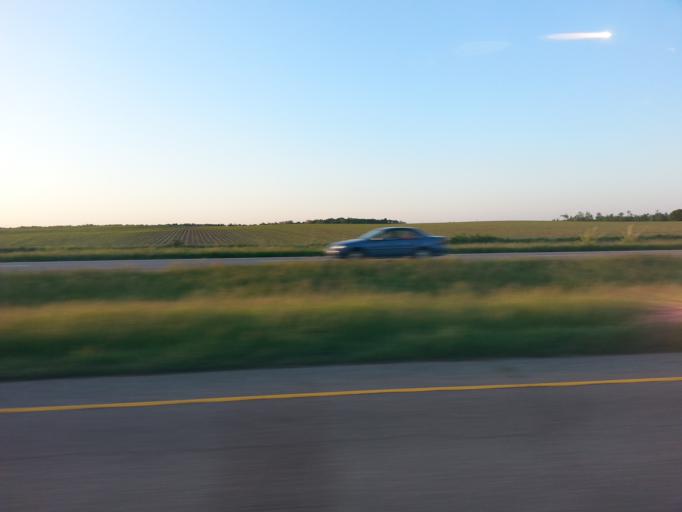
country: US
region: Indiana
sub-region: Fountain County
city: Veedersburg
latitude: 40.1175
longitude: -87.1290
